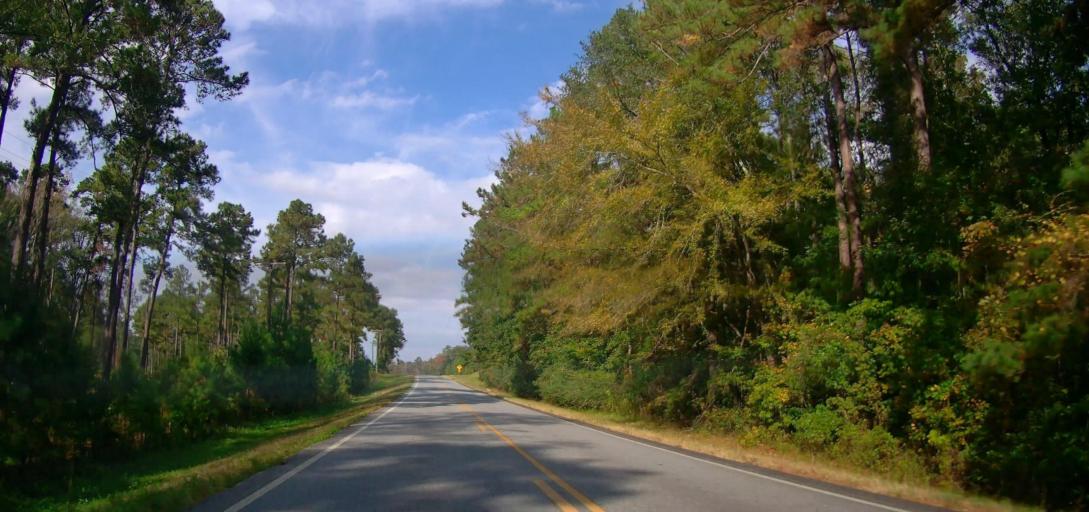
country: US
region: Georgia
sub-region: Thomas County
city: Thomasville
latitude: 30.9049
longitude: -84.0062
